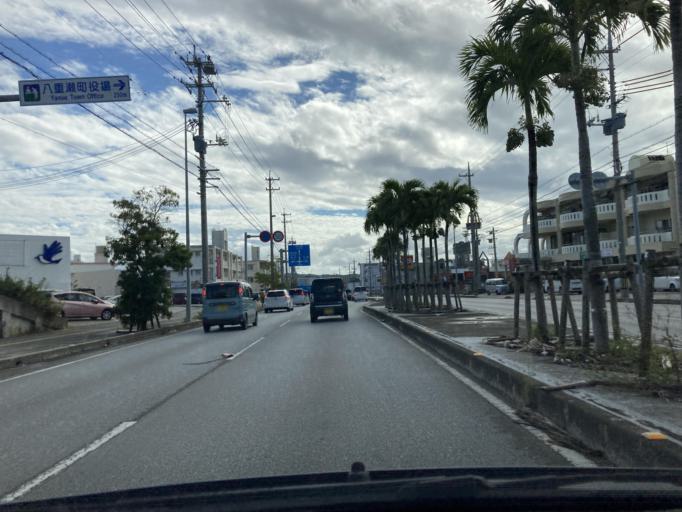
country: JP
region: Okinawa
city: Tomigusuku
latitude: 26.1584
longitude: 127.7218
